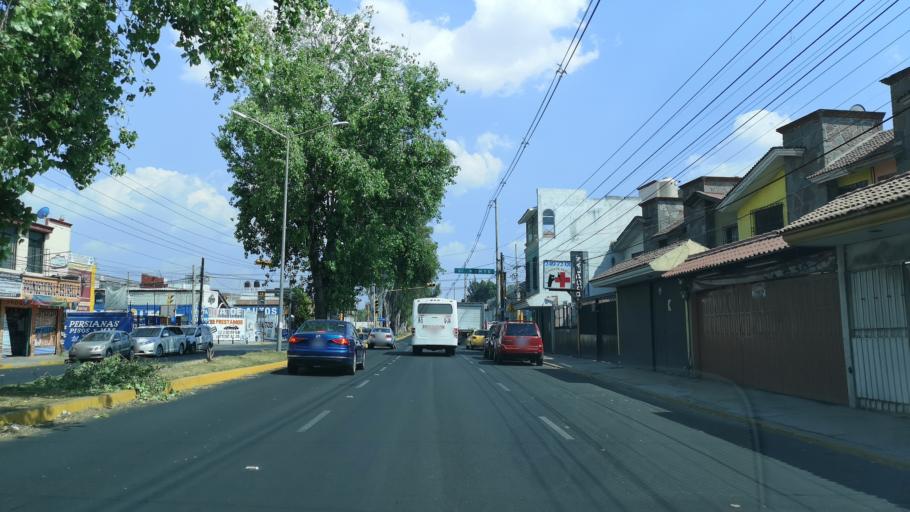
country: MX
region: Puebla
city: Puebla
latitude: 19.0681
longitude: -98.2181
